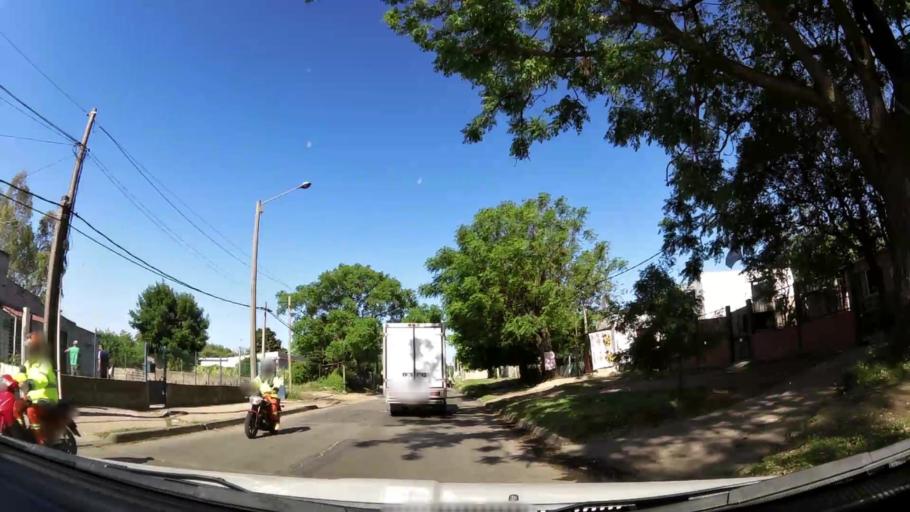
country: UY
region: Montevideo
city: Montevideo
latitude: -34.8341
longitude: -56.1544
